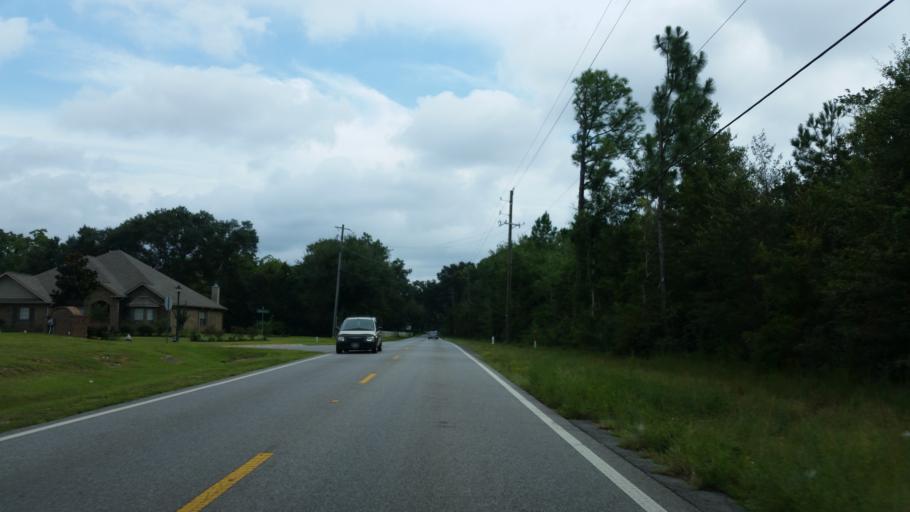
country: US
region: Florida
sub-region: Santa Rosa County
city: Pace
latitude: 30.6410
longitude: -87.1478
